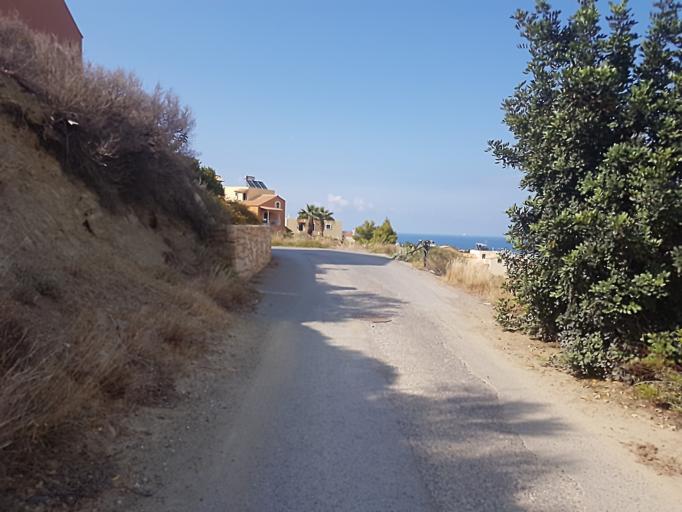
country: GR
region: Crete
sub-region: Nomos Irakleiou
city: Limin Khersonisou
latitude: 35.3141
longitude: 25.3850
